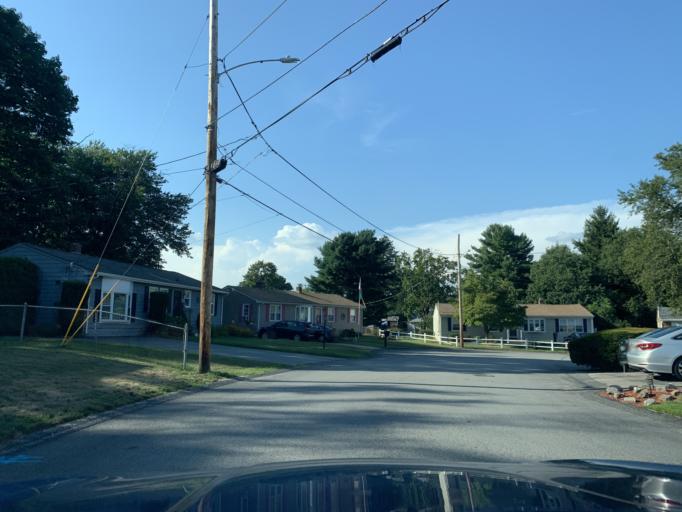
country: US
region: Rhode Island
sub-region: Kent County
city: West Warwick
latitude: 41.6859
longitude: -71.5139
